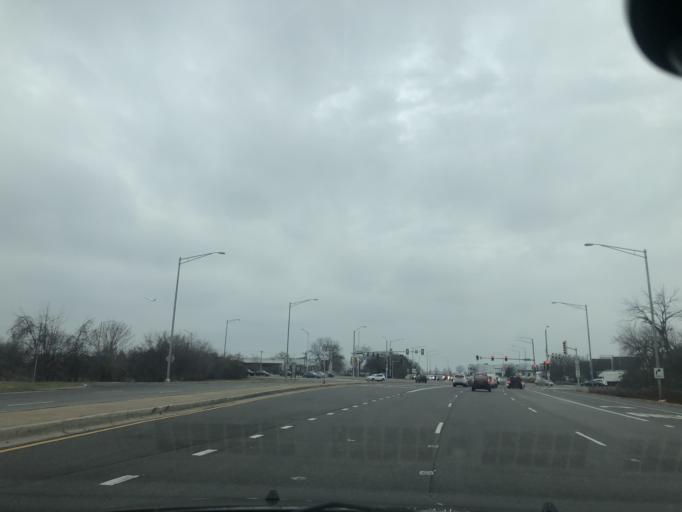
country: US
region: Illinois
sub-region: Cook County
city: Schiller Park
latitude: 41.9572
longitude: -87.8825
